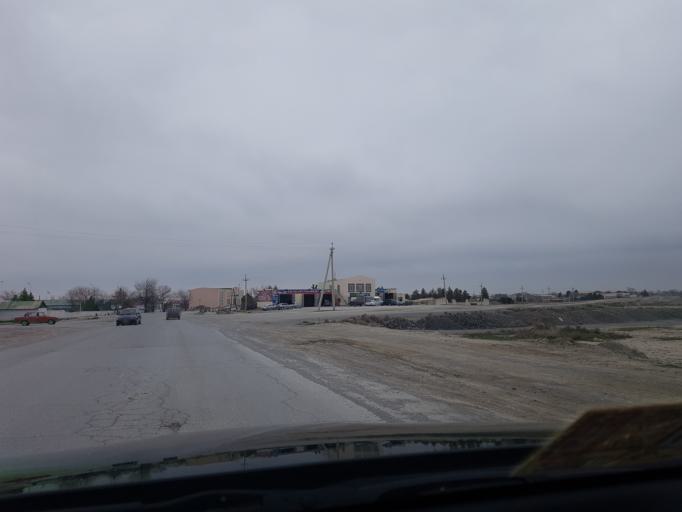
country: TM
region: Ahal
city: Abadan
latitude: 38.1398
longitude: 57.9501
